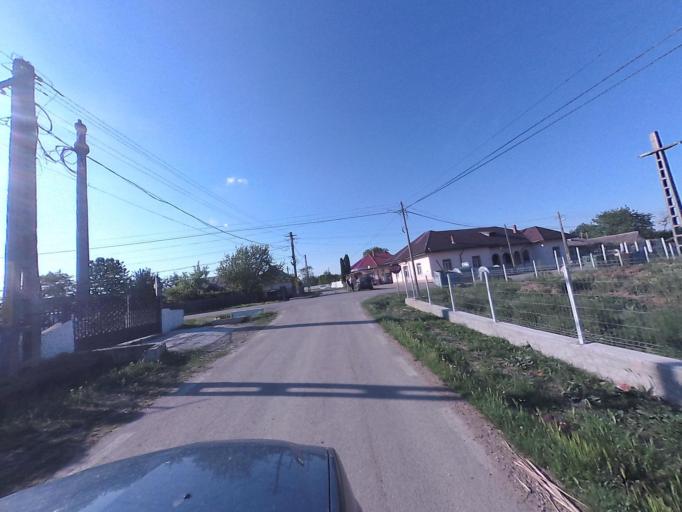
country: RO
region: Neamt
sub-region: Comuna Cordun
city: Pildesti
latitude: 46.9802
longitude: 26.8104
